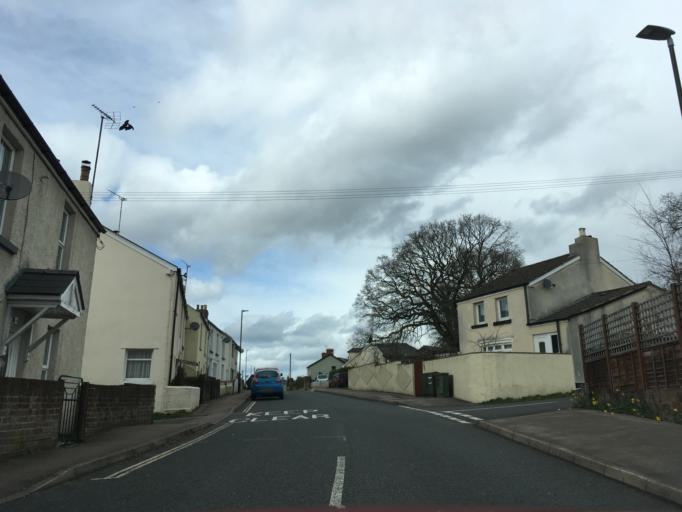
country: GB
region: England
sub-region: Gloucestershire
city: Cinderford
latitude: 51.8131
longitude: -2.5037
